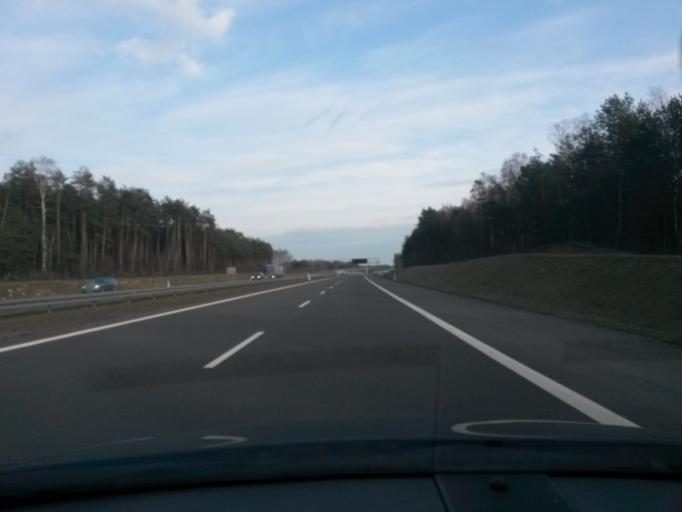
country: PL
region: Lodz Voivodeship
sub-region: Powiat zgierski
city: Zgierz
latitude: 51.9167
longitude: 19.4188
